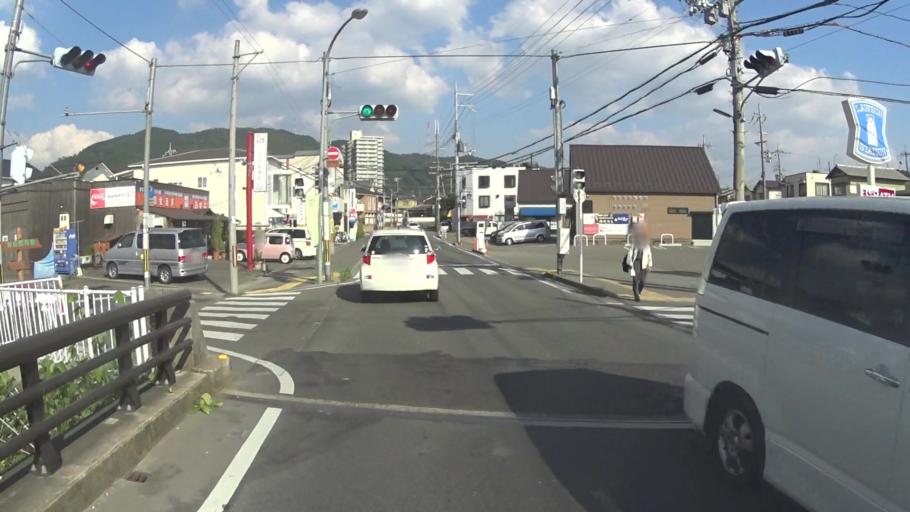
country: JP
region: Kyoto
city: Kameoka
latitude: 35.0095
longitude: 135.5995
